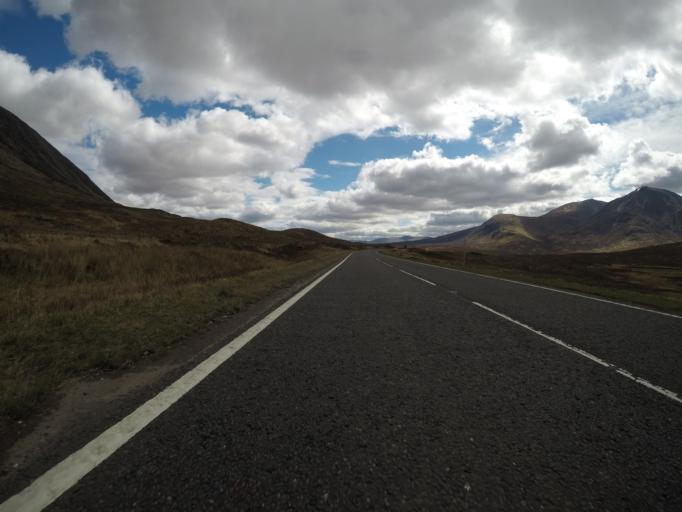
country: GB
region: Scotland
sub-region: Highland
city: Spean Bridge
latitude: 56.6586
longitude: -4.8816
